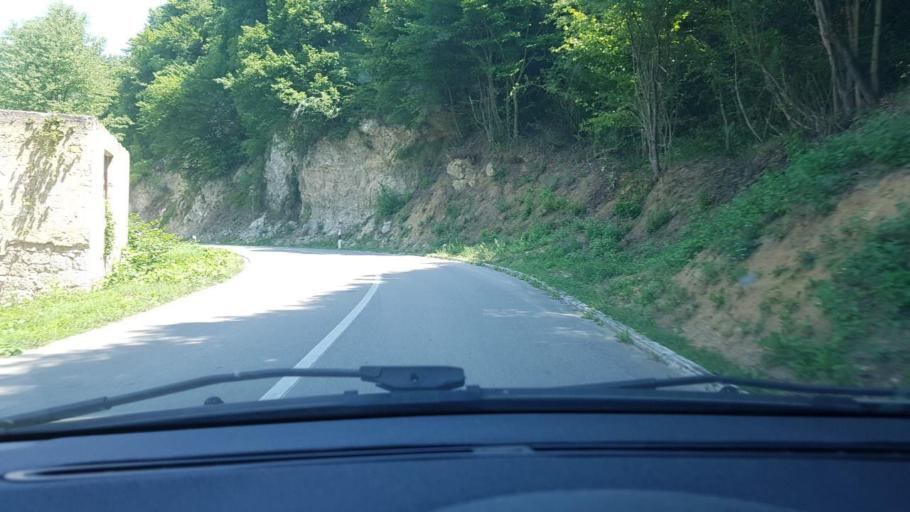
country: BA
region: Federation of Bosnia and Herzegovina
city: Orasac
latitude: 44.5868
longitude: 16.0810
